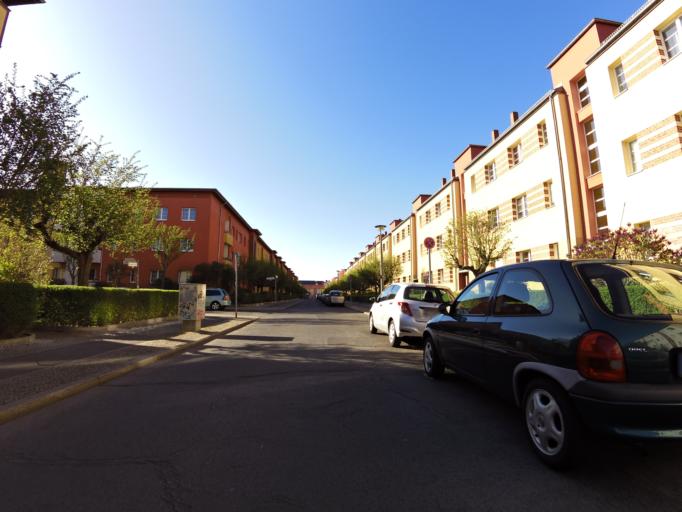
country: DE
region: Berlin
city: Niederschoneweide
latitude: 52.4495
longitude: 13.5144
